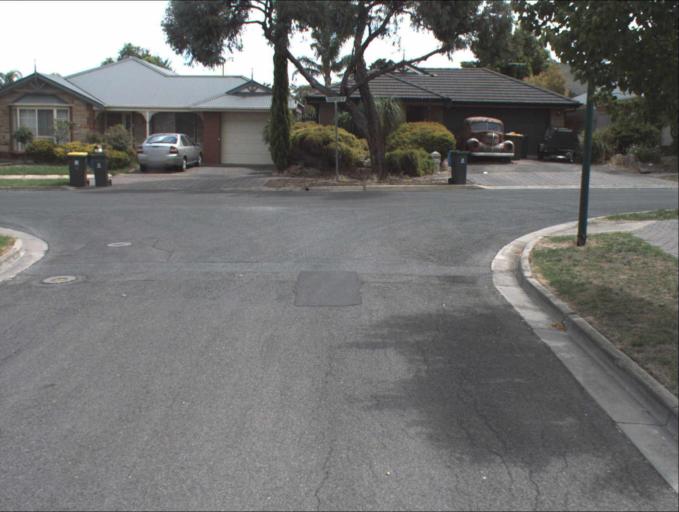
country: AU
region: South Australia
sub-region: Port Adelaide Enfield
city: Gilles Plains
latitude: -34.8588
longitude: 138.6604
